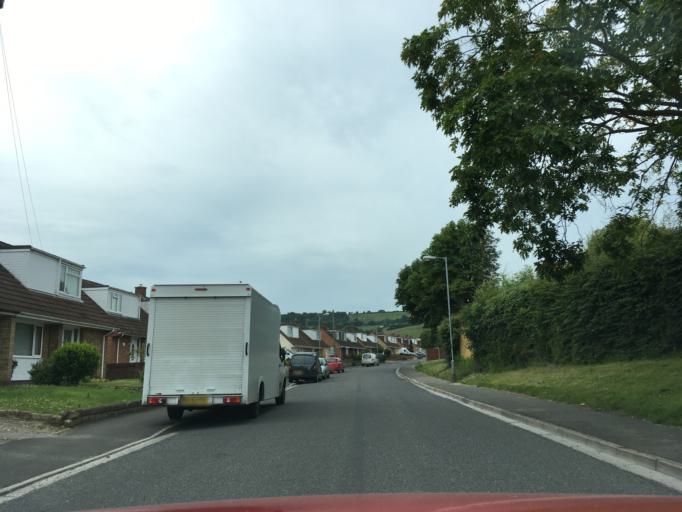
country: GB
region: England
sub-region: Bath and North East Somerset
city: Whitchurch
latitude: 51.4042
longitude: -2.5723
